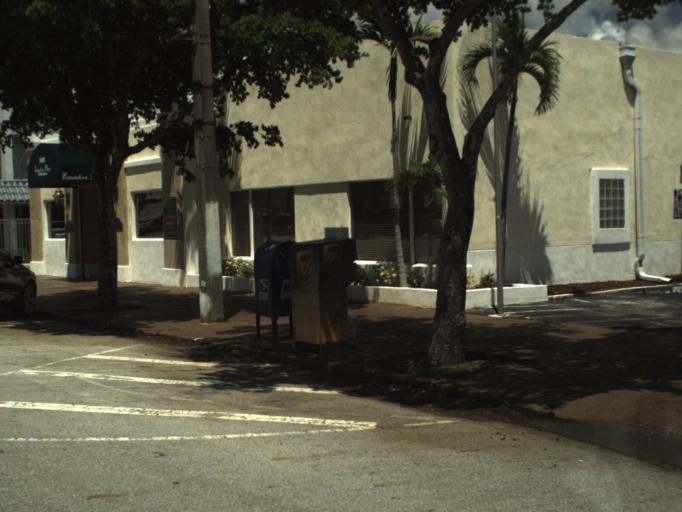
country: US
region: Florida
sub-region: Broward County
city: Hollywood
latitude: 26.0113
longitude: -80.1564
